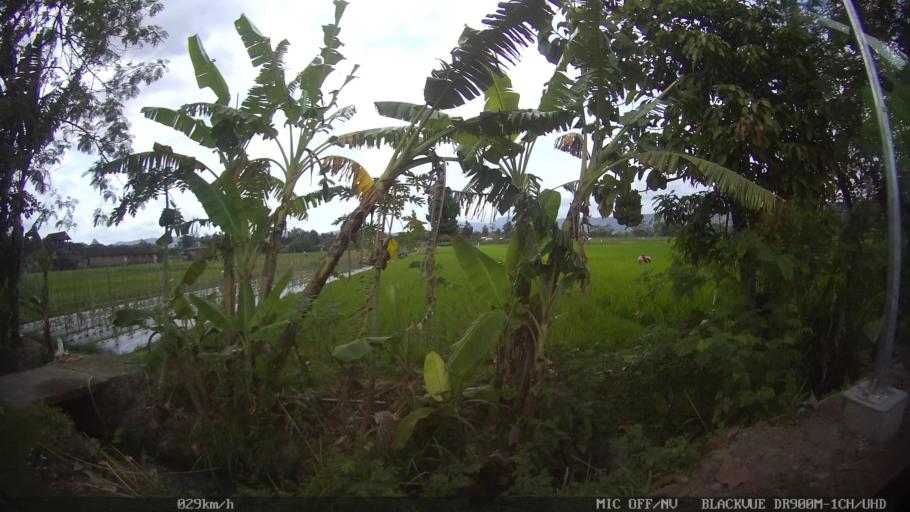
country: ID
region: Daerah Istimewa Yogyakarta
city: Depok
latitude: -7.8168
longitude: 110.4650
